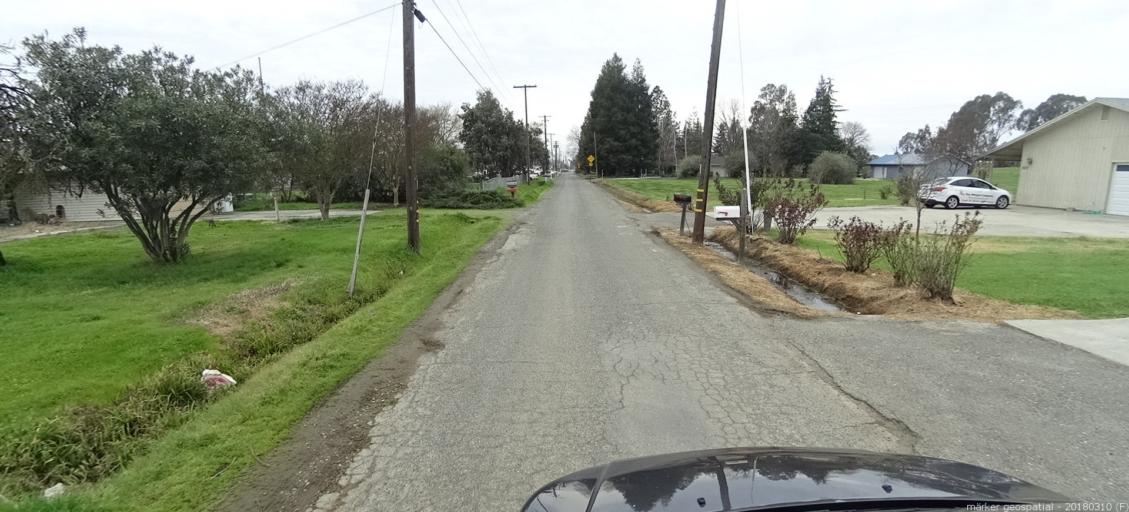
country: US
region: California
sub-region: Sacramento County
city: Vineyard
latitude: 38.4726
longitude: -121.3680
